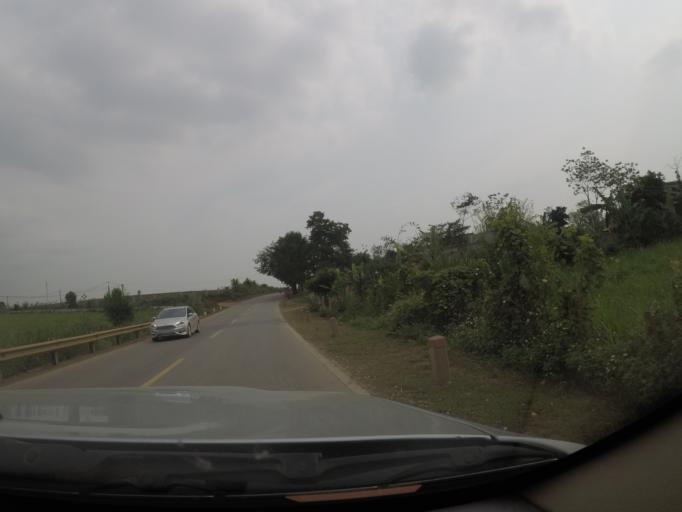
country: VN
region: Thanh Hoa
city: Thi Tran Ben Sung
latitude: 19.3833
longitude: 105.4607
